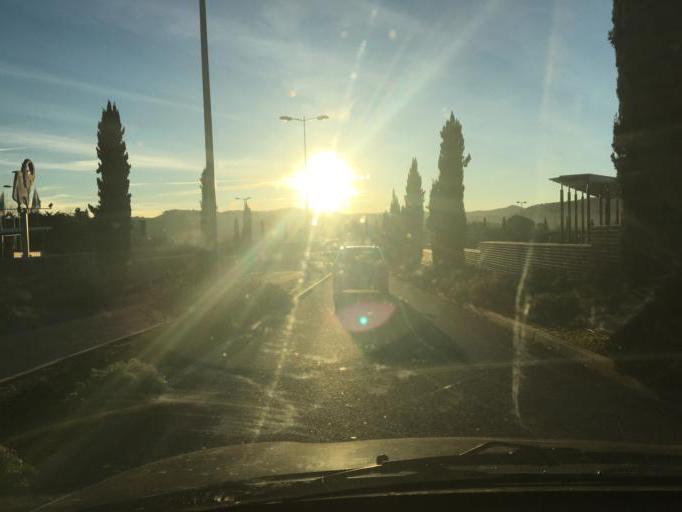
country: FR
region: Provence-Alpes-Cote d'Azur
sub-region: Departement du Var
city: Les Arcs
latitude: 43.4524
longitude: 6.4901
